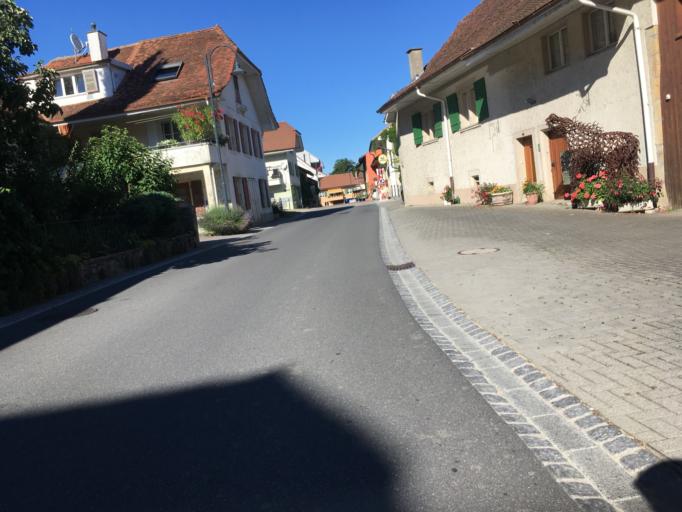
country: CH
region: Fribourg
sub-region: See District
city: Bas-Vully
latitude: 46.9480
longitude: 7.0825
